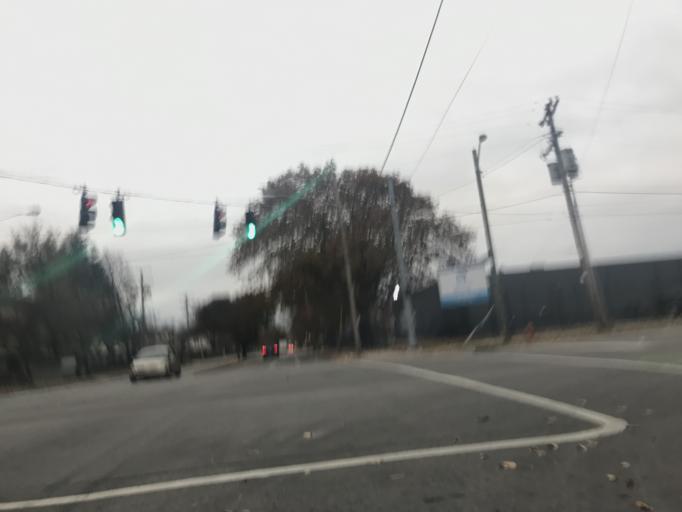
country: US
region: Kentucky
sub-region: Jefferson County
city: Louisville
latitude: 38.2556
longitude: -85.7720
